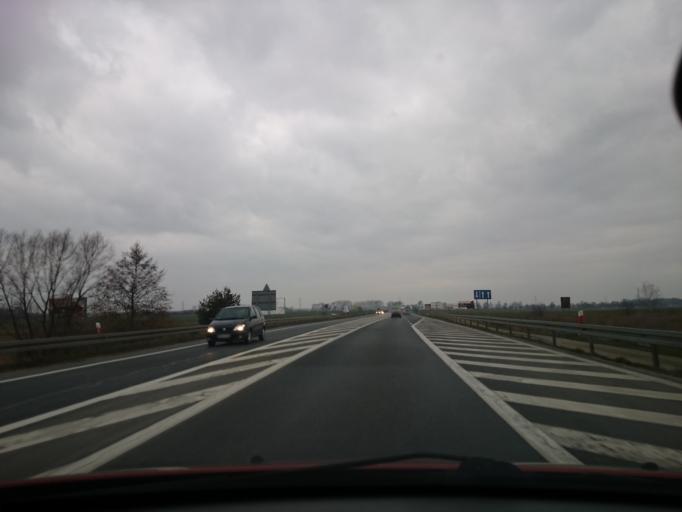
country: PL
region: Opole Voivodeship
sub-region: Powiat opolski
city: Chroscina
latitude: 50.6889
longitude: 17.8067
